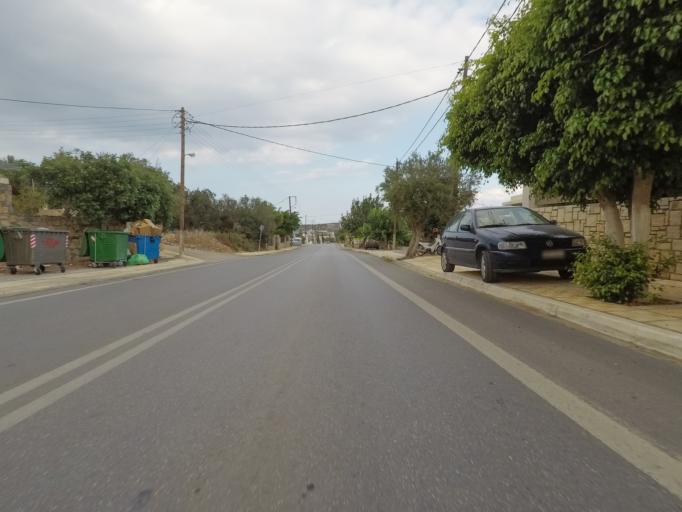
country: GR
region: Crete
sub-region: Nomos Lasithiou
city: Agios Nikolaos
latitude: 35.1801
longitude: 25.6938
